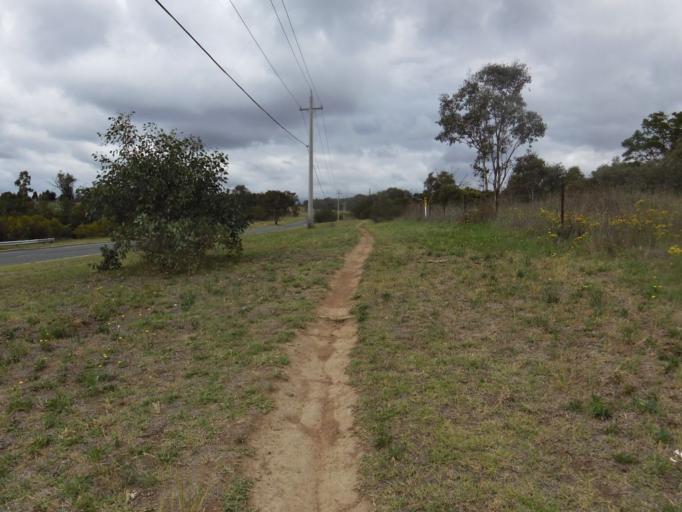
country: AU
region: Australian Capital Territory
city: Macquarie
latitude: -35.3262
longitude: 149.0265
